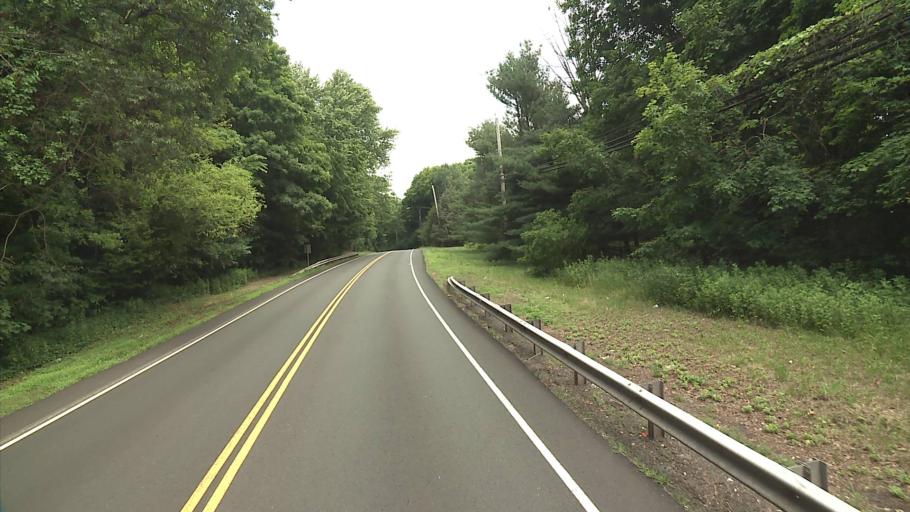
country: US
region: Connecticut
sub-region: New Haven County
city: North Branford
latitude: 41.3865
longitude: -72.7940
